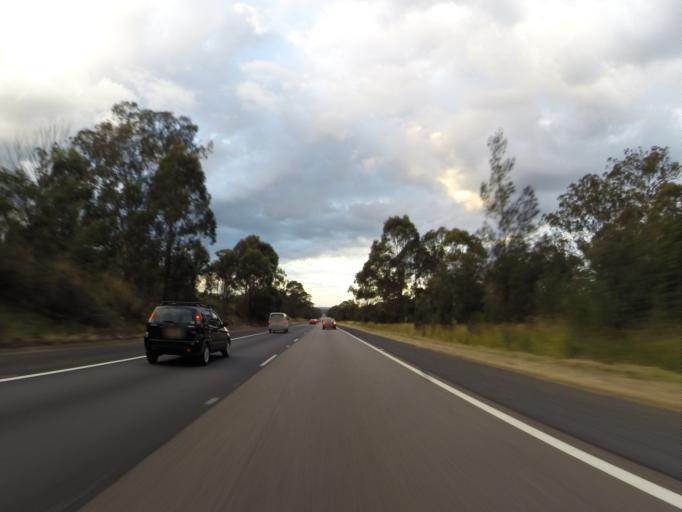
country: AU
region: New South Wales
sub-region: Wollondilly
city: Douglas Park
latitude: -34.2151
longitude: 150.6840
